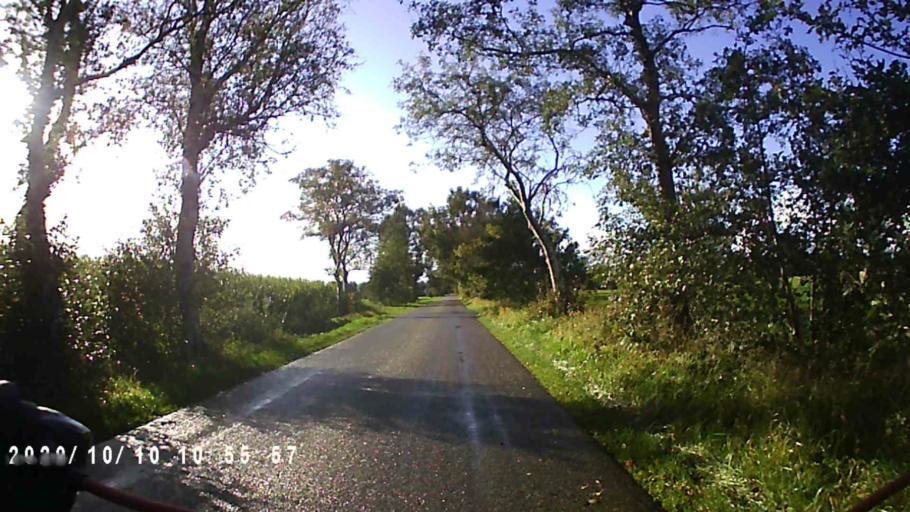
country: NL
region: Friesland
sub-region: Gemeente Achtkarspelen
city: Surhuisterveen
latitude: 53.1533
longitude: 6.2066
